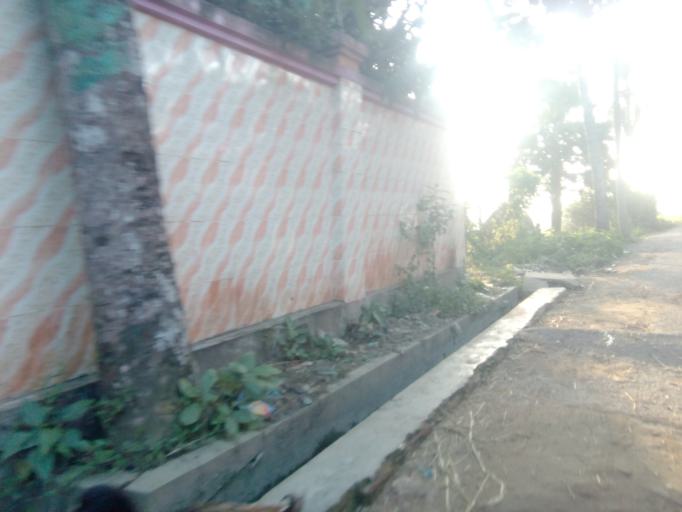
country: BD
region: Chittagong
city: Comilla
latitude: 23.4147
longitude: 91.2017
